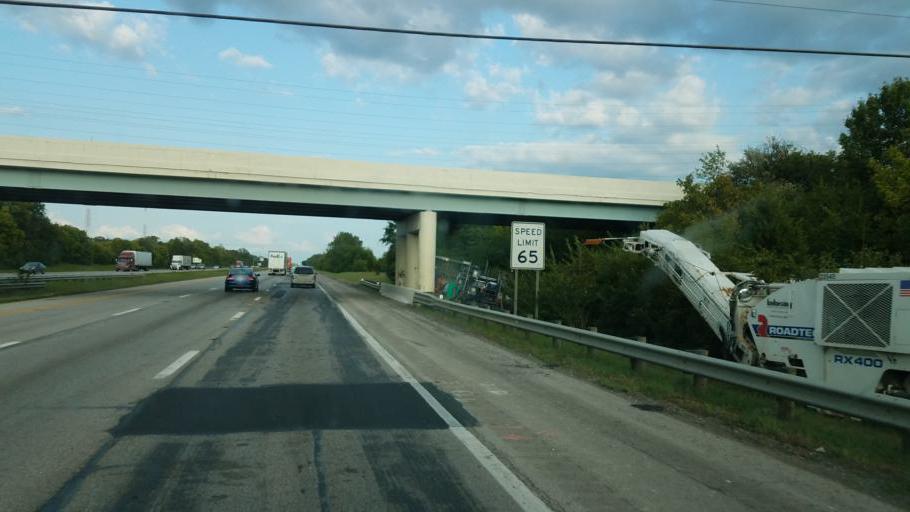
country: US
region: Ohio
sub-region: Franklin County
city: Obetz
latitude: 39.8734
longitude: -82.9891
